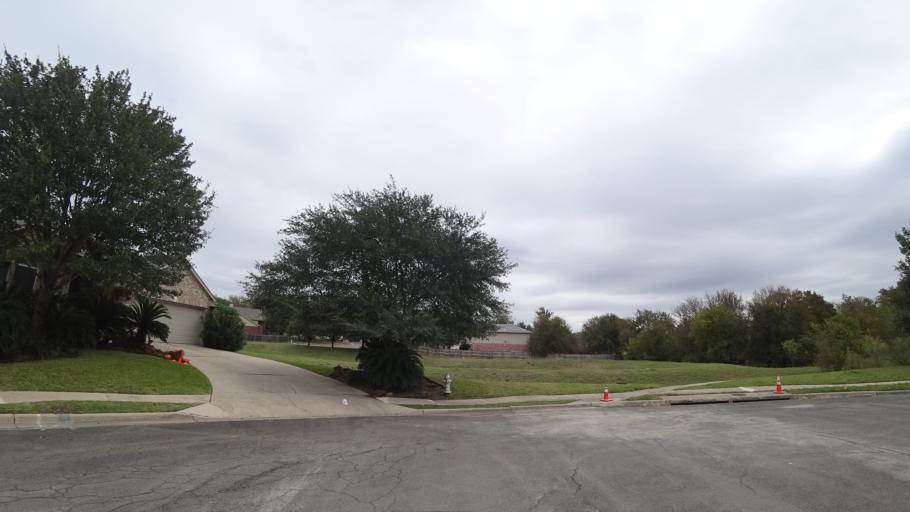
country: US
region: Texas
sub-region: Travis County
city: Shady Hollow
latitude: 30.1520
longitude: -97.8549
